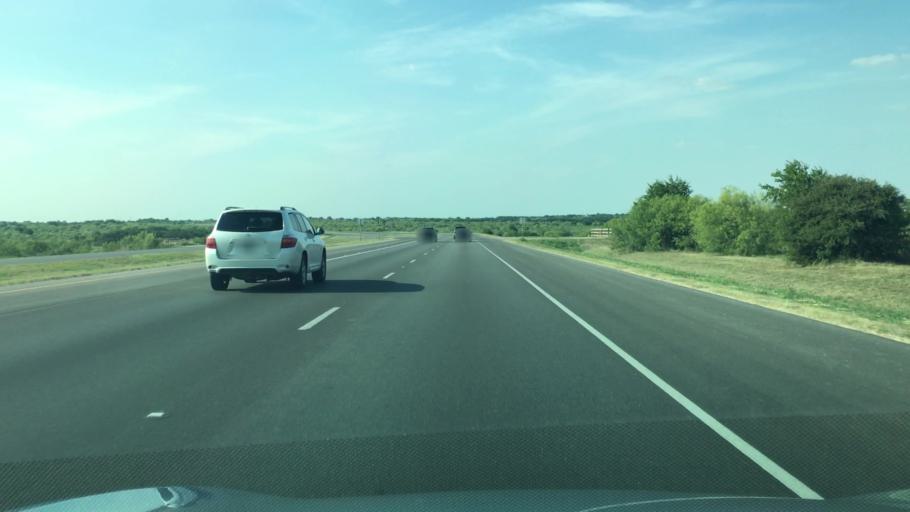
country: US
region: Texas
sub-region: Hays County
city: Kyle
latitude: 30.0333
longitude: -97.8723
